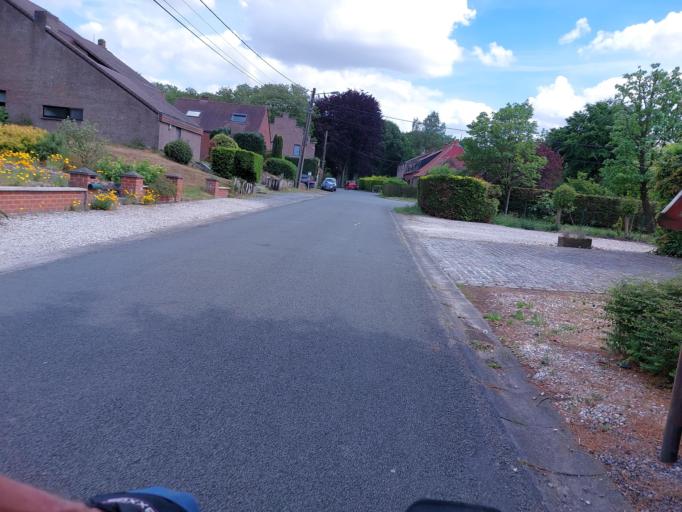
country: BE
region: Wallonia
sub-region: Province du Hainaut
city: Saint-Ghislain
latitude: 50.4914
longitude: 3.8004
